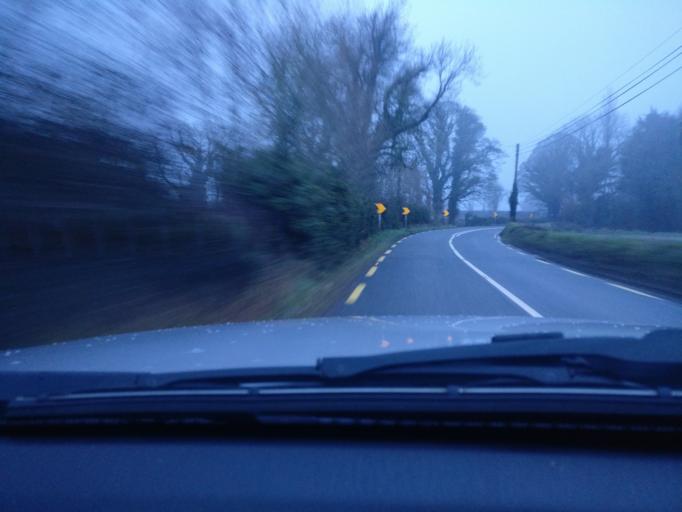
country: IE
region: Leinster
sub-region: An Mhi
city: Athboy
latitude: 53.6145
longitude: -6.9433
